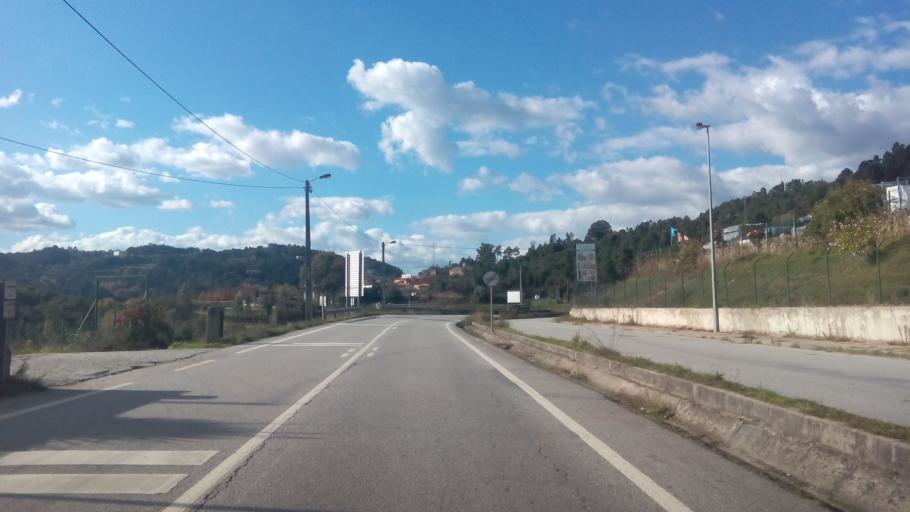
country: PT
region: Porto
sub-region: Amarante
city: Amarante
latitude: 41.2518
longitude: -8.0379
